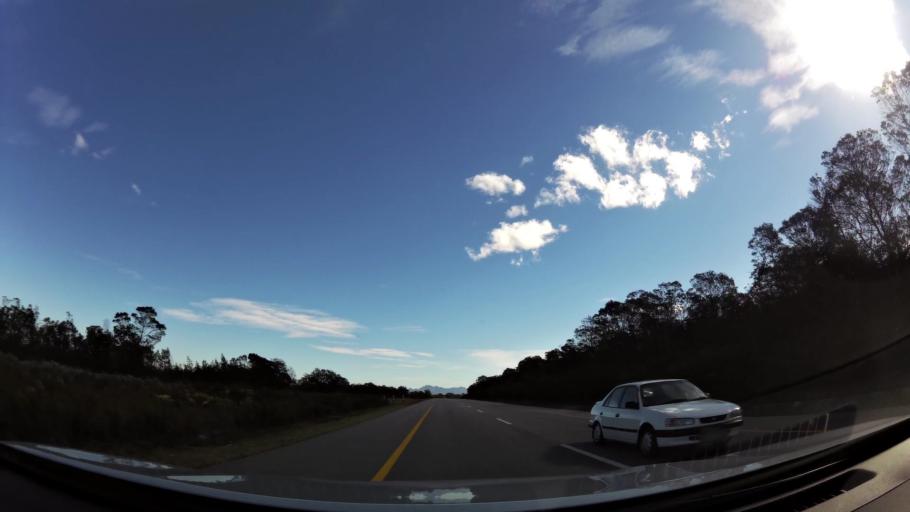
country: ZA
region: Eastern Cape
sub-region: Cacadu District Municipality
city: Kruisfontein
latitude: -33.9954
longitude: 24.7142
